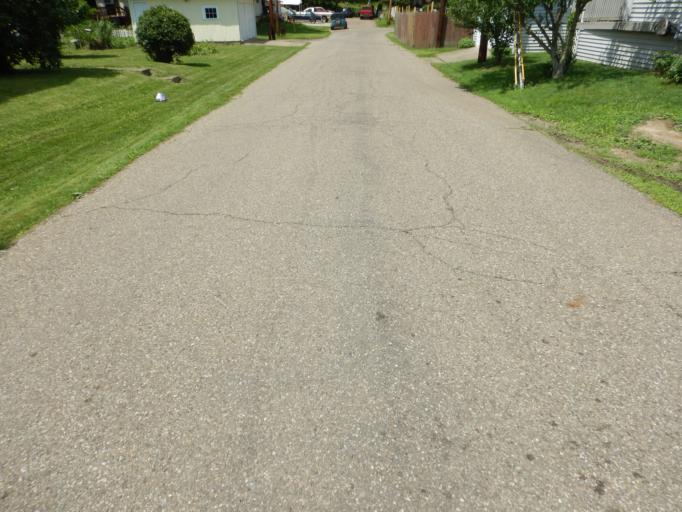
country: US
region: Ohio
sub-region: Muskingum County
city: Zanesville
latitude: 39.9204
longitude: -82.0115
